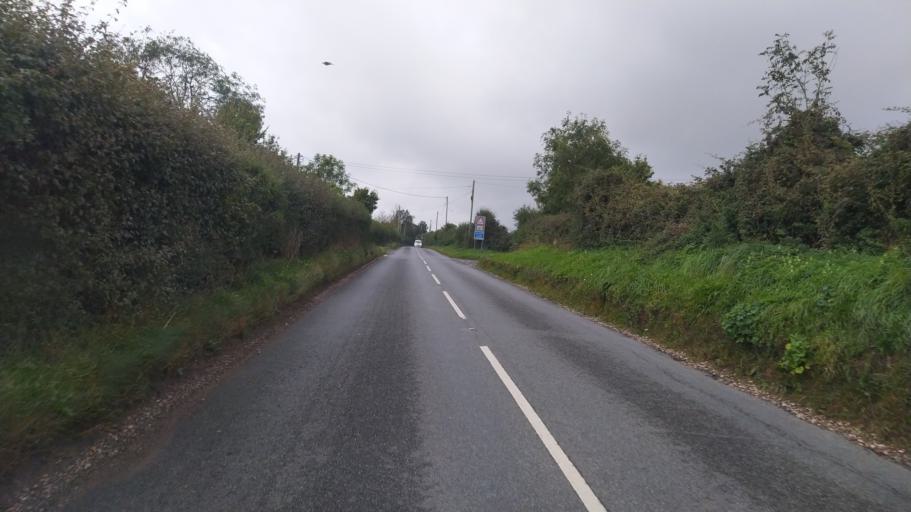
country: GB
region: England
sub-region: Wiltshire
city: Salisbury
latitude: 51.1148
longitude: -1.7560
